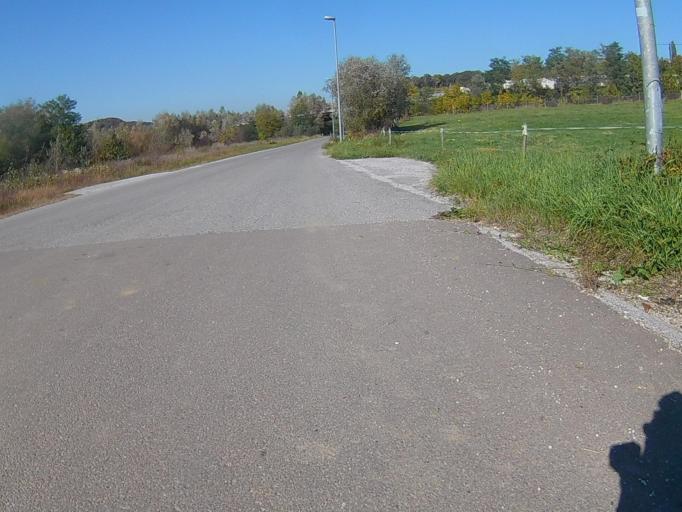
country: SI
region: Sveti Jurij v Slovenskih Goricah
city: Jurovski Dol
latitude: 46.5706
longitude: 15.7605
